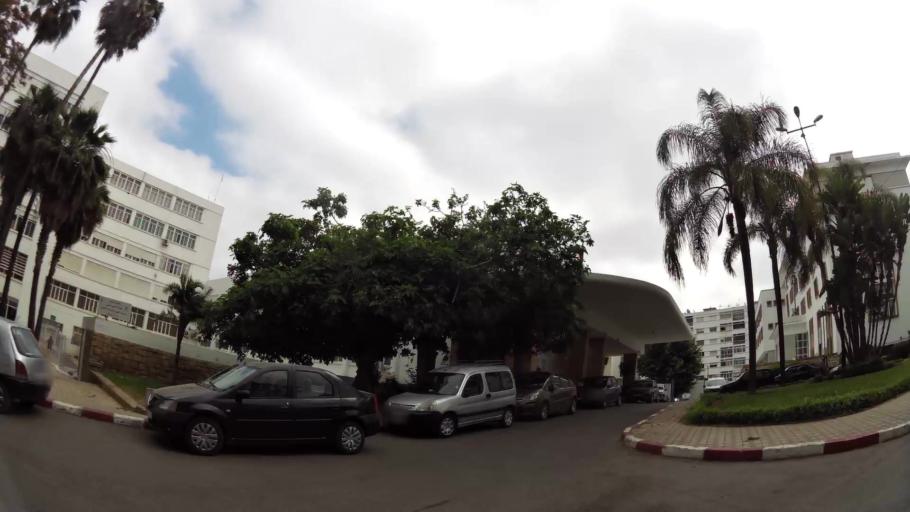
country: MA
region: Rabat-Sale-Zemmour-Zaer
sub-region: Rabat
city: Rabat
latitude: 34.0185
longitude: -6.8324
